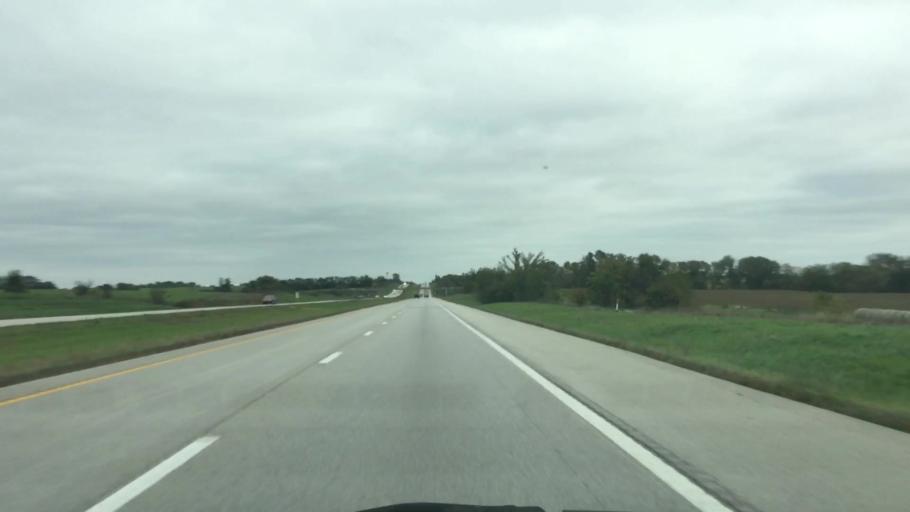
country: US
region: Missouri
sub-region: Clinton County
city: Cameron
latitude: 39.7981
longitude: -94.2012
